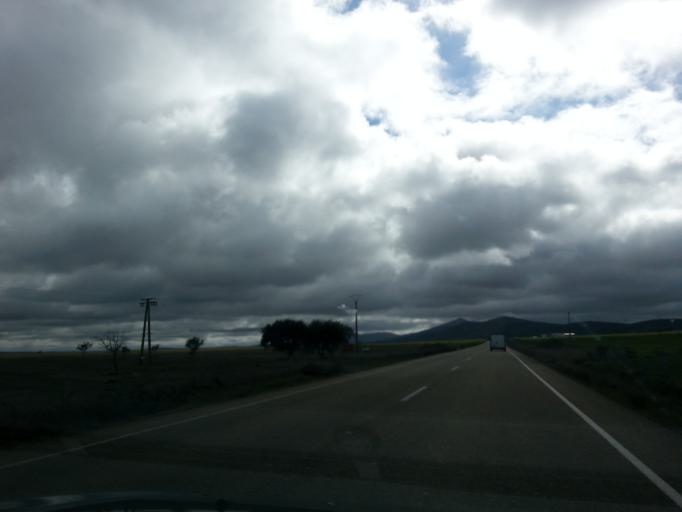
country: ES
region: Castille and Leon
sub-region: Provincia de Salamanca
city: Tamames
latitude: 40.6733
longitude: -6.1224
